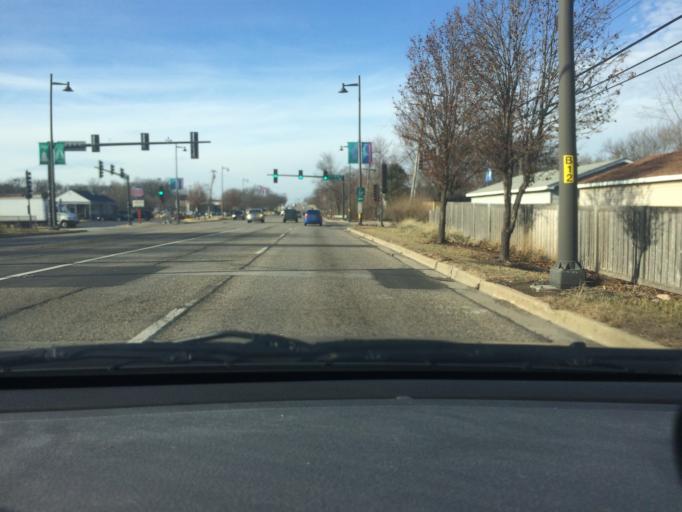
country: US
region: Illinois
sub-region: Cook County
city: Streamwood
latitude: 42.0121
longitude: -88.1751
